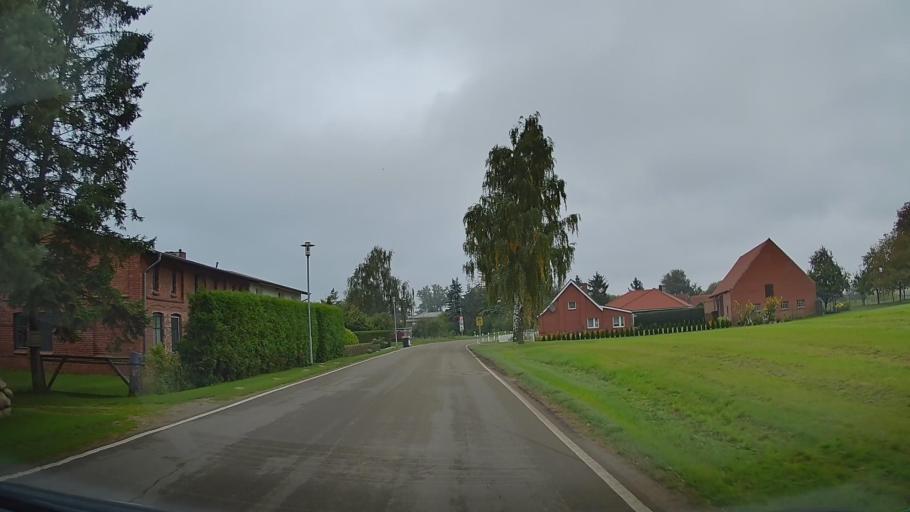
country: DE
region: Mecklenburg-Vorpommern
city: Blowatz
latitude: 53.9764
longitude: 11.5513
